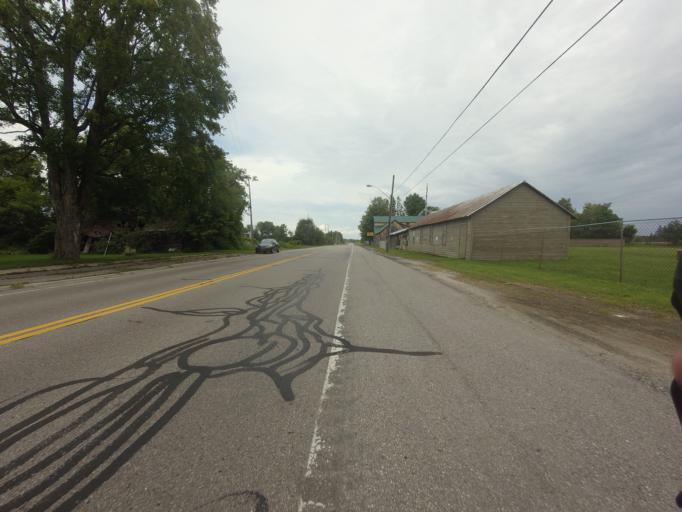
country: CA
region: Ontario
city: Perth
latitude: 45.0984
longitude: -76.3949
